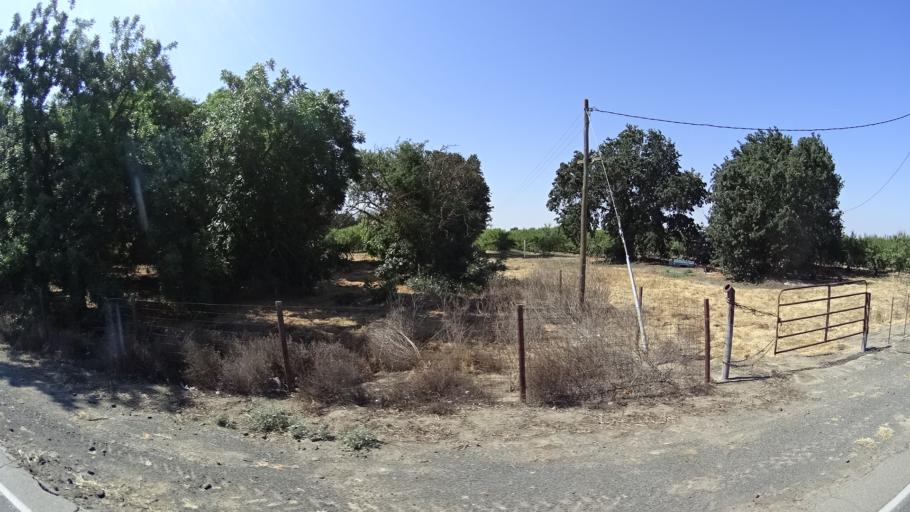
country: US
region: California
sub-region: Kings County
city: Lemoore
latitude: 36.3440
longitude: -119.8304
